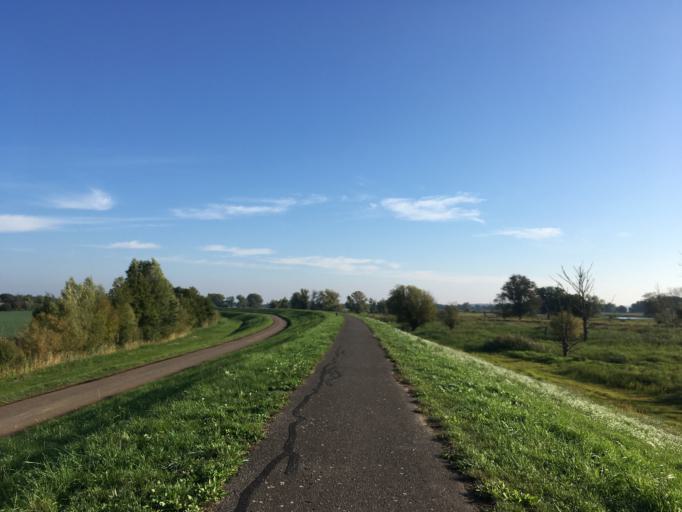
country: DE
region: Brandenburg
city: Reitwein
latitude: 52.4524
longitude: 14.5869
